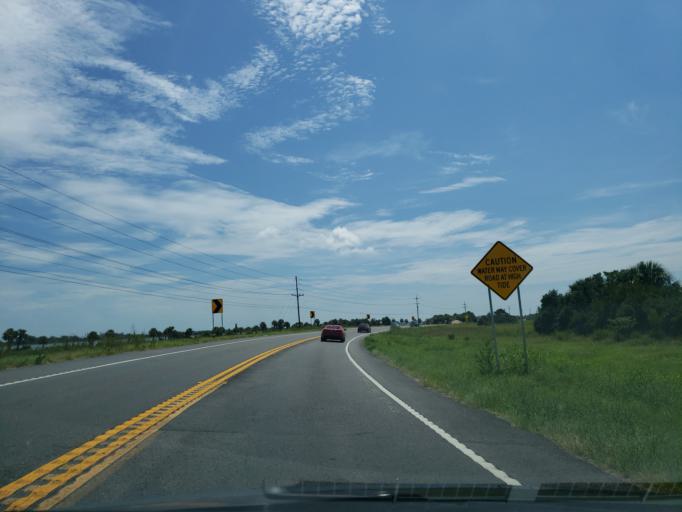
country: US
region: Georgia
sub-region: Chatham County
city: Wilmington Island
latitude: 32.0408
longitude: -80.9478
